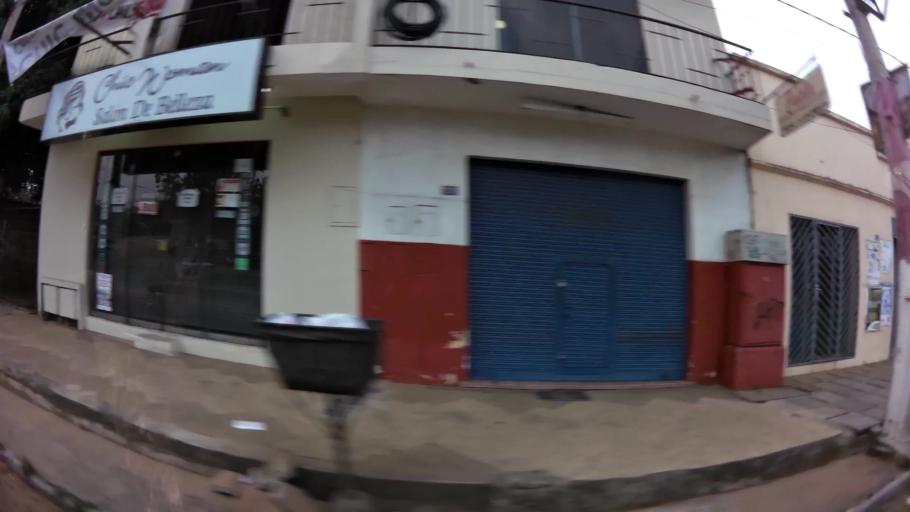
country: PY
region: Central
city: Lambare
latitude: -25.3430
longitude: -57.6089
